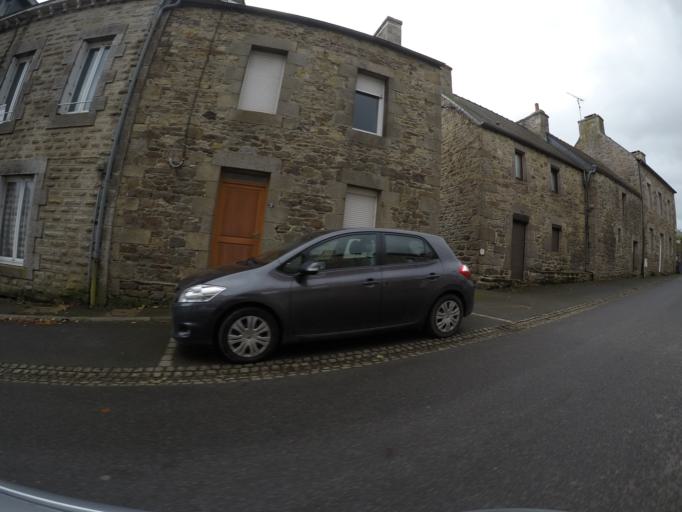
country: FR
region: Brittany
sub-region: Departement des Cotes-d'Armor
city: Bourbriac
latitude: 48.4730
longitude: -3.1882
